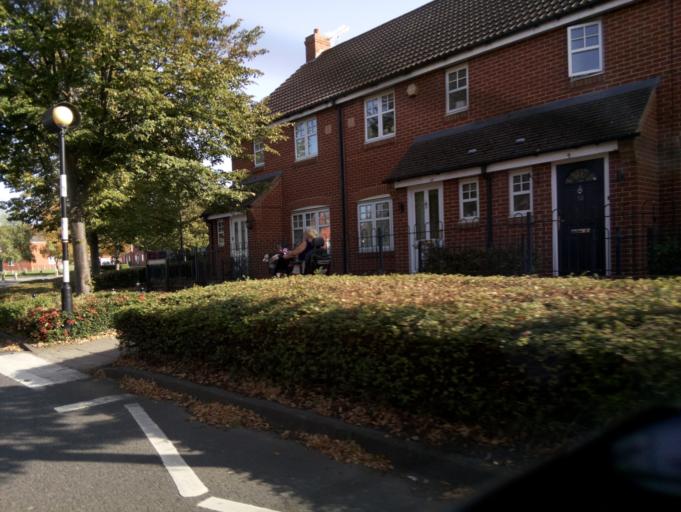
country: GB
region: England
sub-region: Gloucestershire
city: Tewkesbury
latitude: 51.9809
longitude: -2.1427
